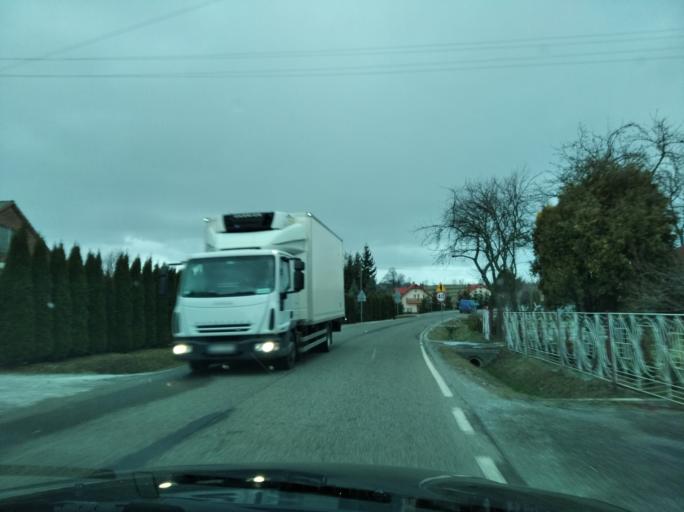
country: PL
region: Subcarpathian Voivodeship
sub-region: Powiat rzeszowski
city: Hyzne
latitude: 49.9312
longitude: 22.1863
